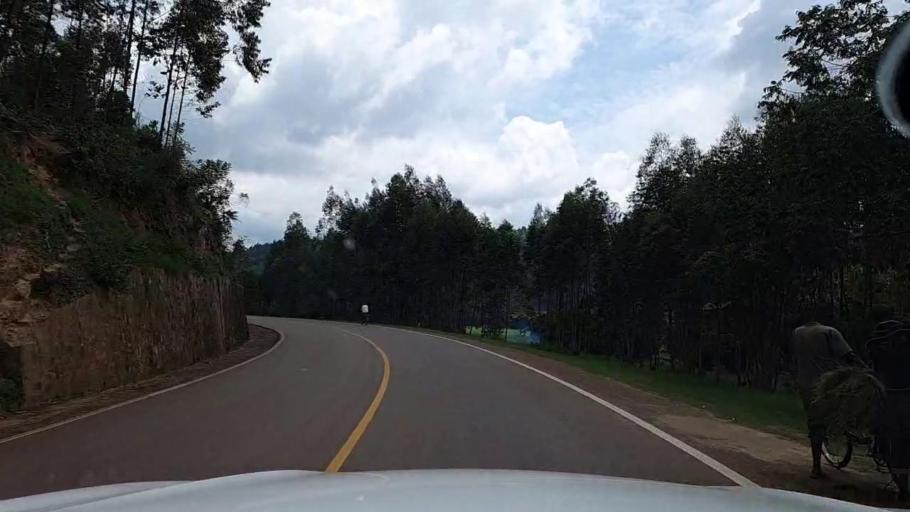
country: RW
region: Kigali
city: Kigali
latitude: -1.8199
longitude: 30.1138
